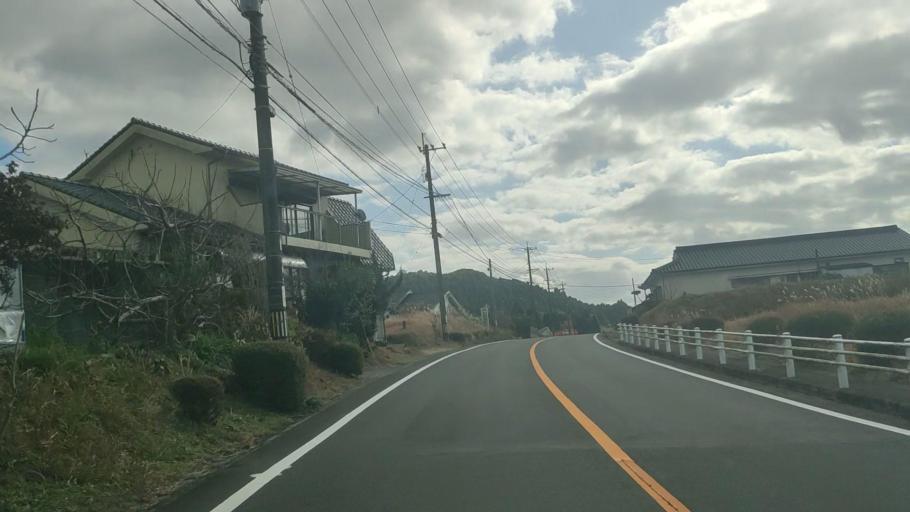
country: JP
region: Kagoshima
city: Kajiki
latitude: 31.8344
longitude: 130.6875
